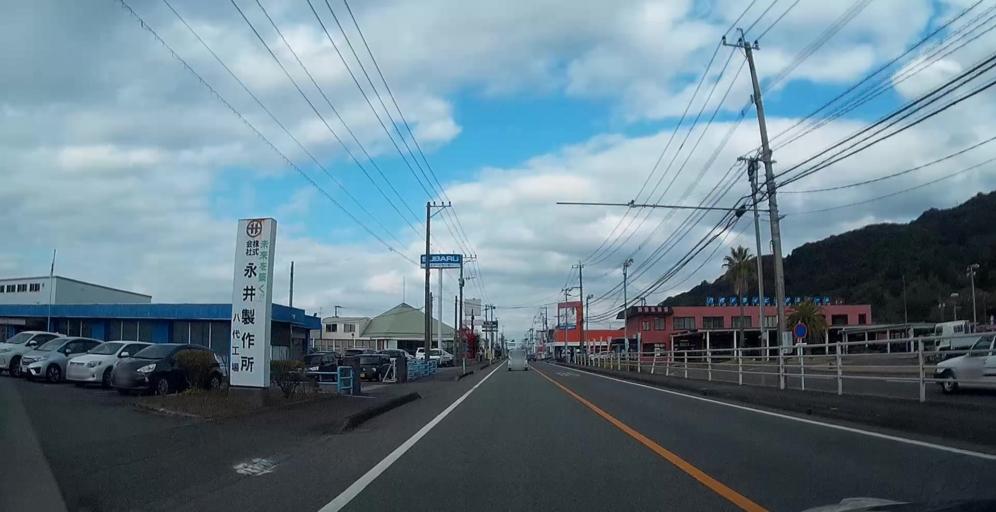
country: JP
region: Kumamoto
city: Yatsushiro
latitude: 32.4688
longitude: 130.6063
